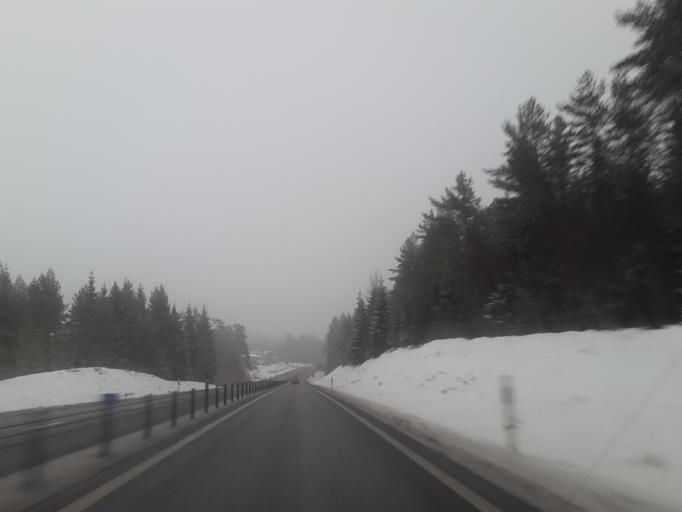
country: SE
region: Joenkoeping
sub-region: Mullsjo Kommun
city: Mullsjoe
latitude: 57.7666
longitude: 13.8182
